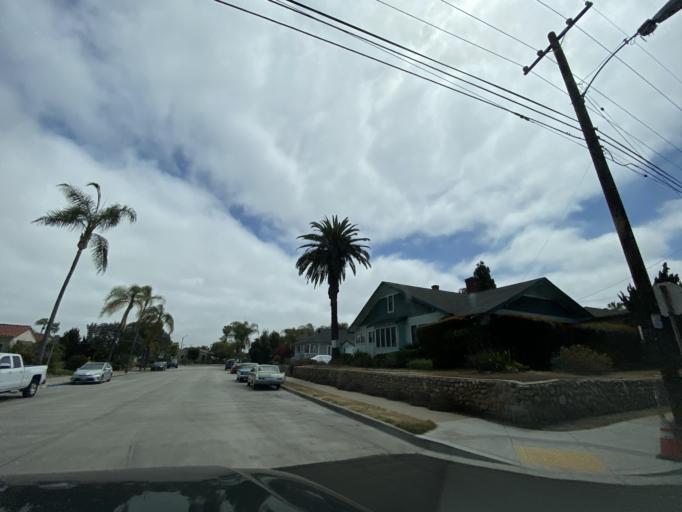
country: US
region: California
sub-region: San Diego County
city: San Diego
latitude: 32.7420
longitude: -117.1229
